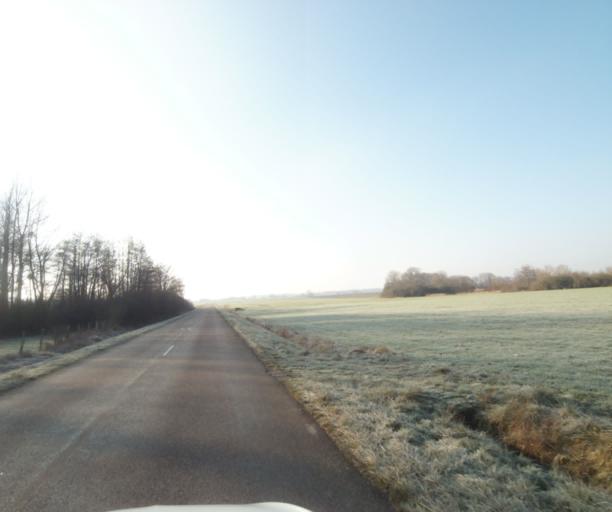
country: FR
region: Champagne-Ardenne
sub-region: Departement de la Haute-Marne
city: Montier-en-Der
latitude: 48.4218
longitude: 4.7459
